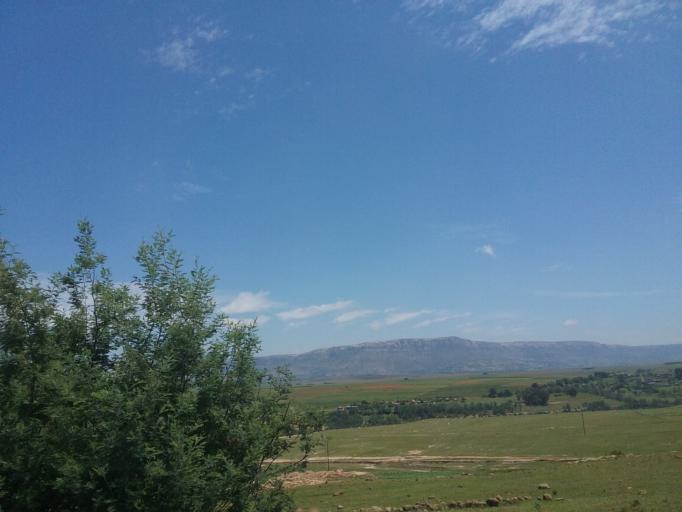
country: LS
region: Maseru
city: Maseru
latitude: -29.4691
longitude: 27.5798
